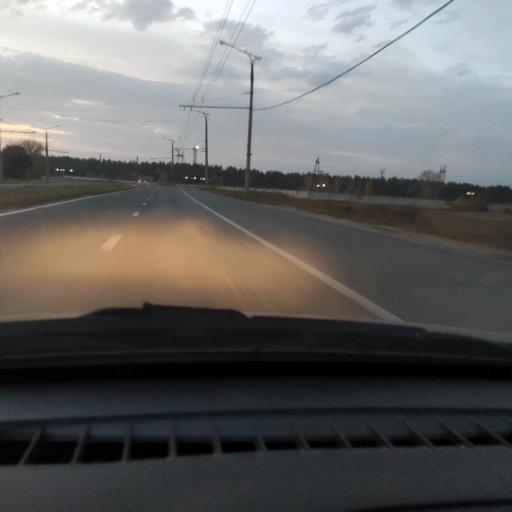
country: RU
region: Samara
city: Povolzhskiy
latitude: 53.5467
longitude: 49.6024
